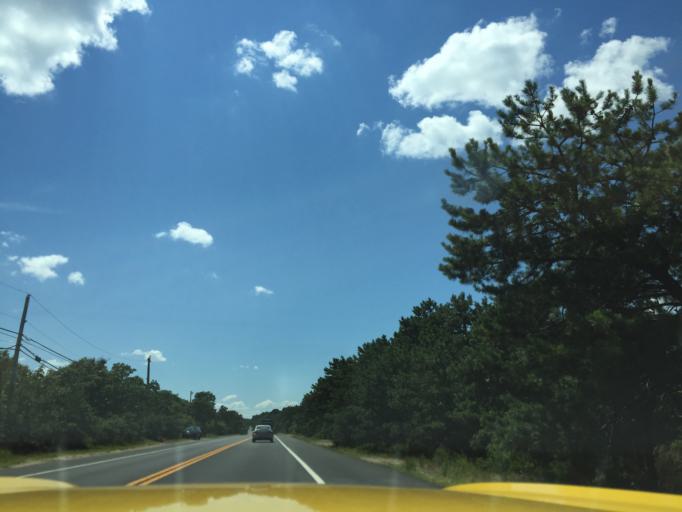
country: US
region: New York
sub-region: Suffolk County
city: Amagansett
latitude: 40.9817
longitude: -72.1037
